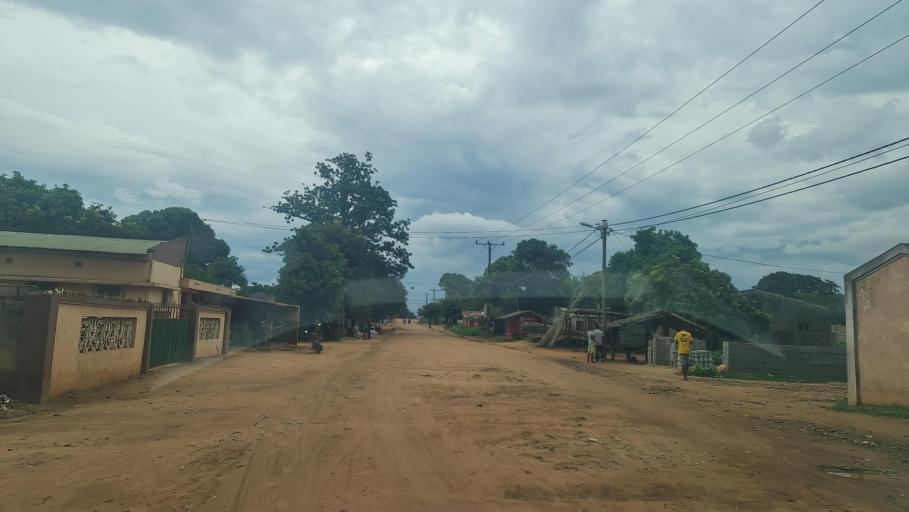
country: MW
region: Southern Region
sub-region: Nsanje District
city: Nsanje
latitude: -17.3324
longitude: 35.5953
